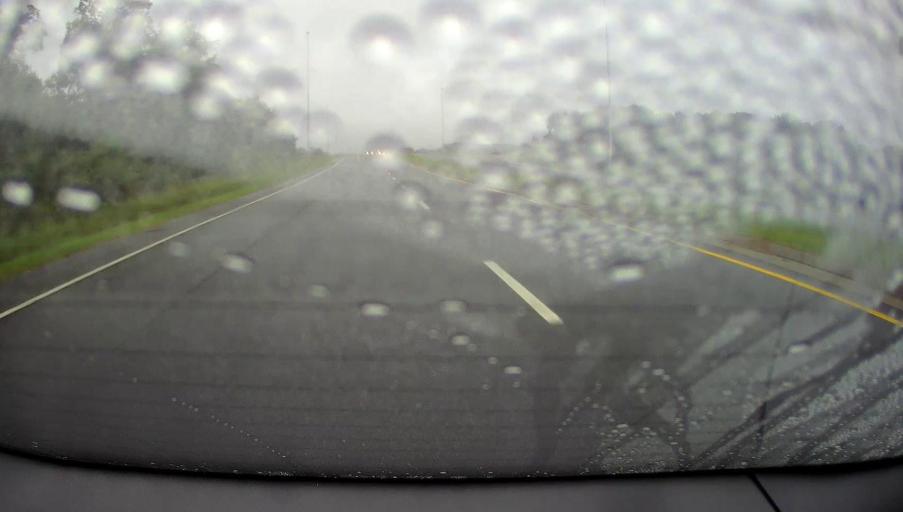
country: US
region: Georgia
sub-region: Houston County
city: Robins Air Force Base
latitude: 32.5519
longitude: -83.5895
